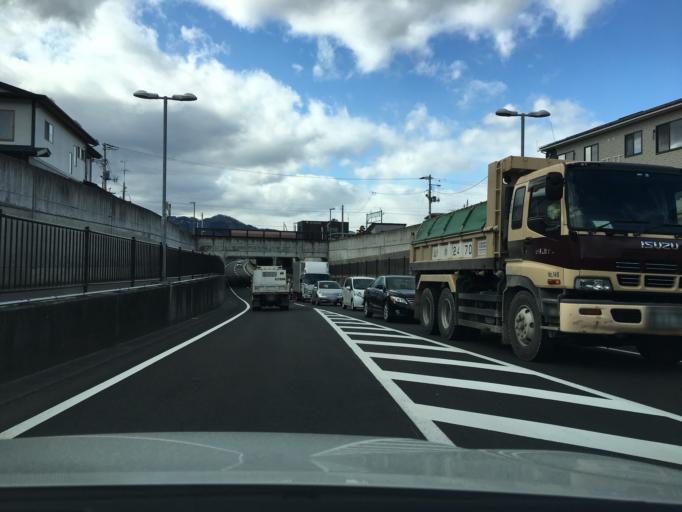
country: JP
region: Yamagata
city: Kaminoyama
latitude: 38.2078
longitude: 140.3055
